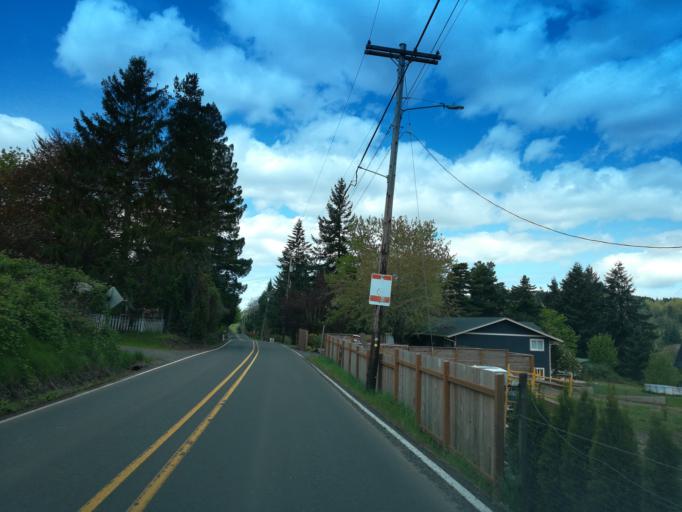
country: US
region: Oregon
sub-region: Clackamas County
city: Damascus
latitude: 45.4345
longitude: -122.4400
